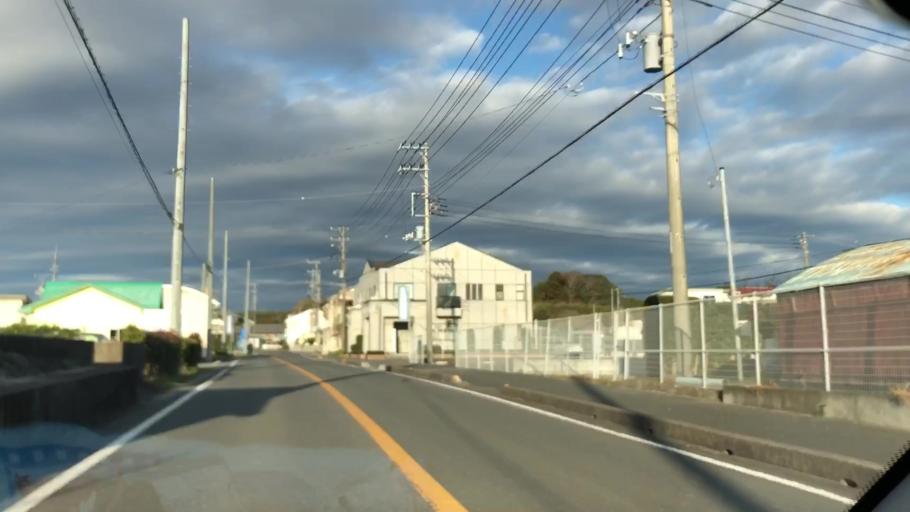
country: JP
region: Chiba
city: Tateyama
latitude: 34.9751
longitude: 139.9586
